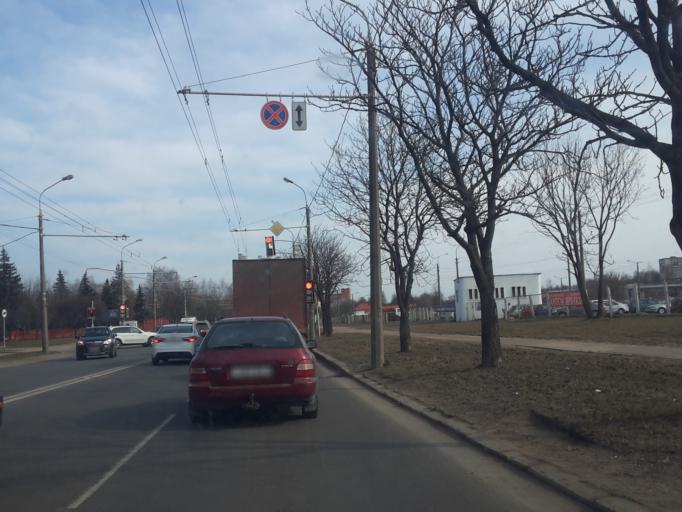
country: BY
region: Minsk
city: Novoye Medvezhino
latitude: 53.8979
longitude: 27.5069
